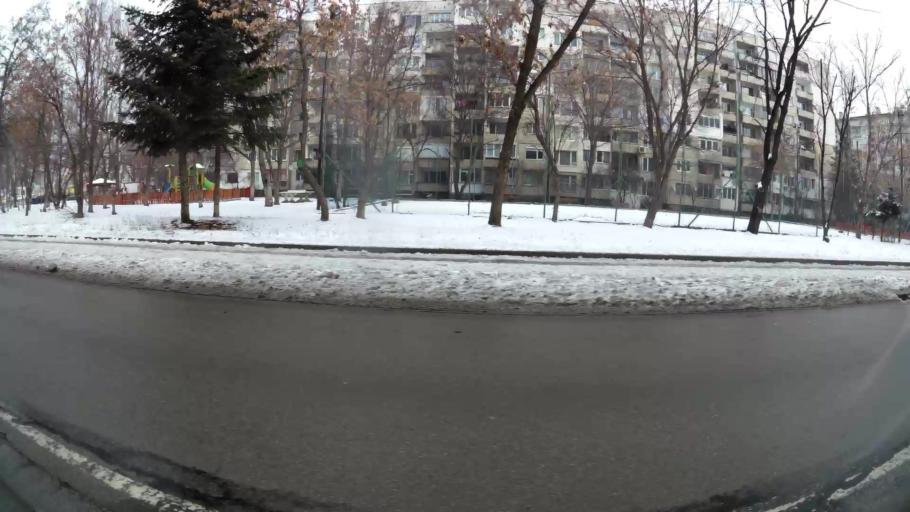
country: BG
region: Sofia-Capital
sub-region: Stolichna Obshtina
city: Sofia
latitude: 42.7086
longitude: 23.3117
